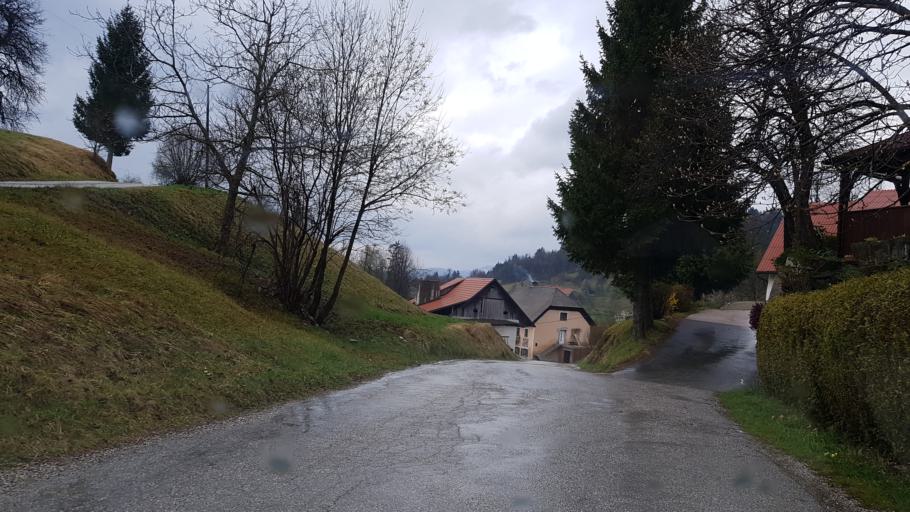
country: SI
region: Tolmin
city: Tolmin
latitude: 46.1376
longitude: 13.8242
